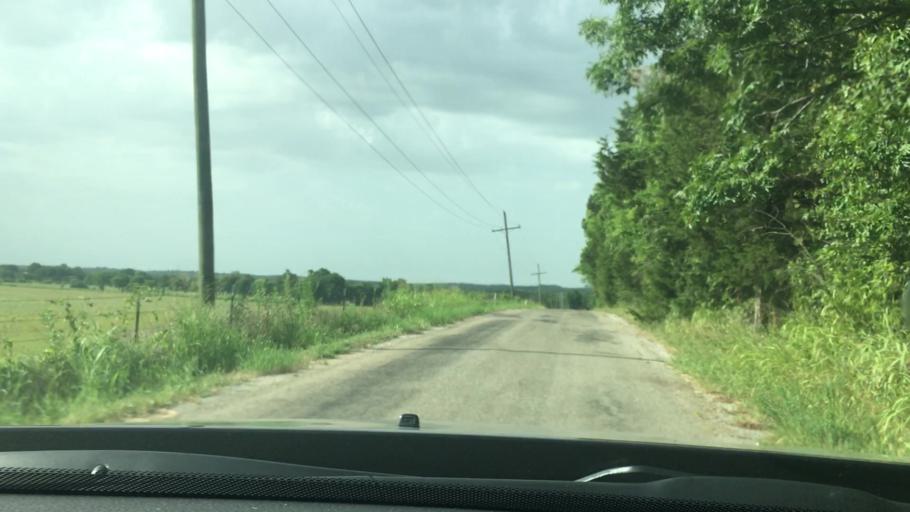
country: US
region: Oklahoma
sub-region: Pontotoc County
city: Byng
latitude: 34.8729
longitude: -96.5785
